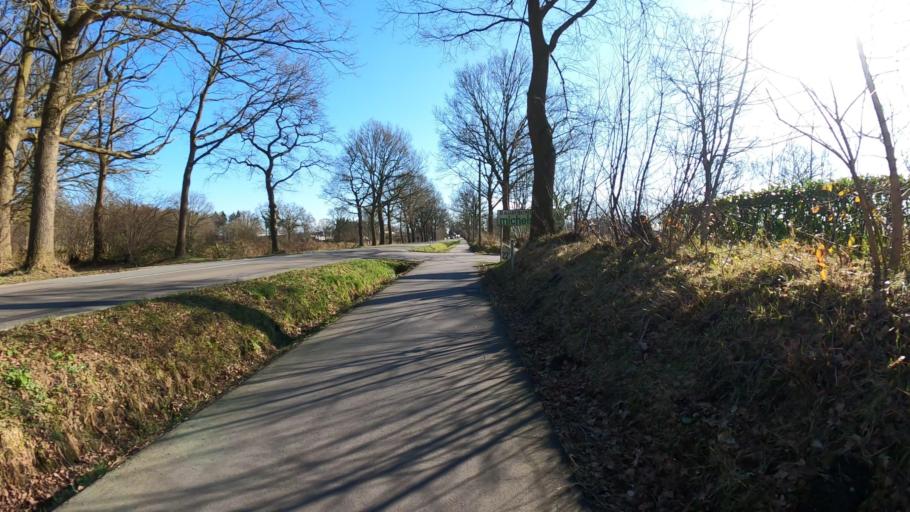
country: DE
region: Schleswig-Holstein
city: Rellingen
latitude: 53.6265
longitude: 9.7961
